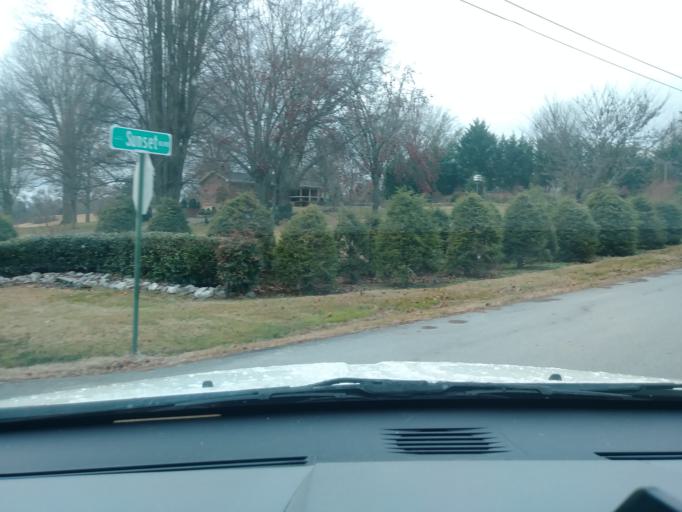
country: US
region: Tennessee
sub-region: Greene County
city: Greeneville
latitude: 36.1374
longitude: -82.8539
